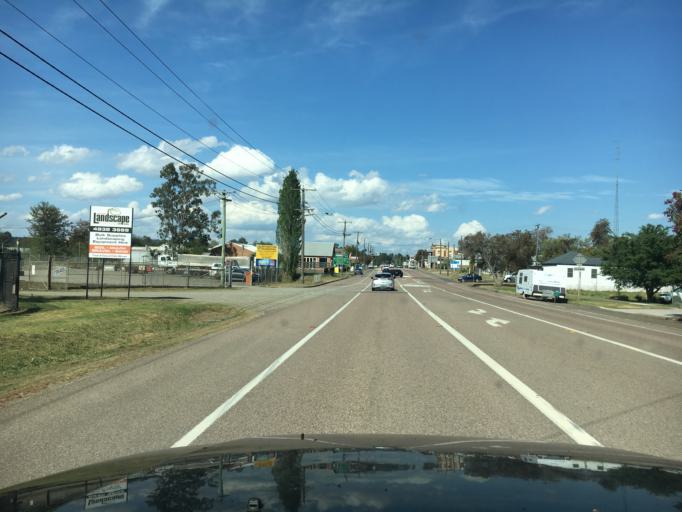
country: AU
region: New South Wales
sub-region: Cessnock
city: Branxton
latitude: -32.6559
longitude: 151.3483
